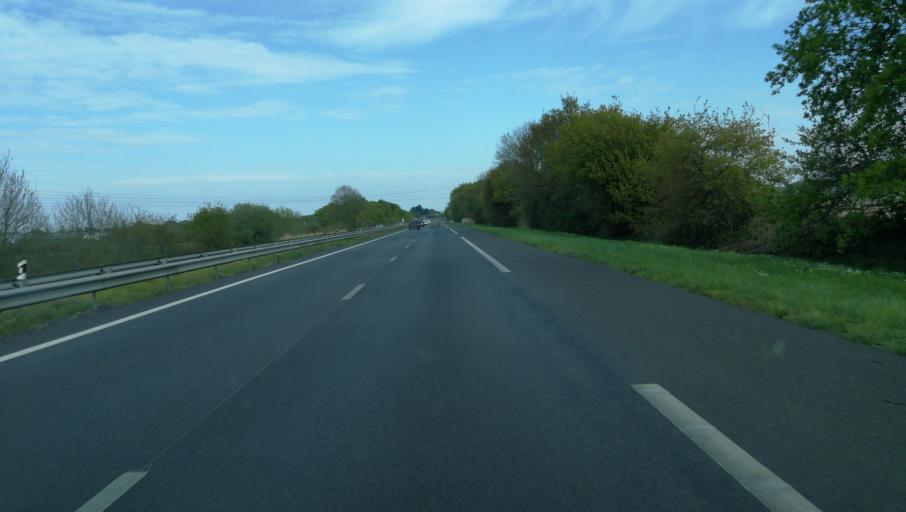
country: FR
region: Pays de la Loire
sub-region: Departement de la Loire-Atlantique
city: Prinquiau
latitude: 47.3570
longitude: -2.0181
